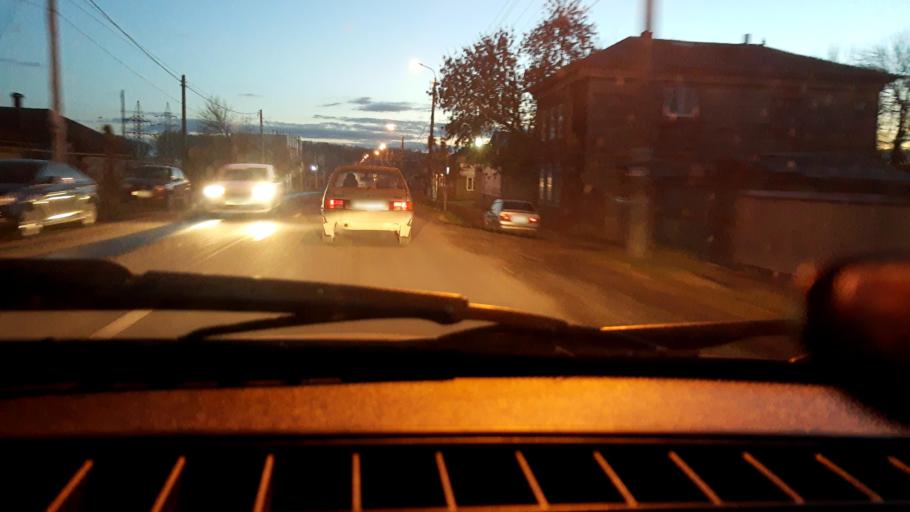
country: RU
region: Bashkortostan
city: Ufa
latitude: 54.7308
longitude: 55.9144
